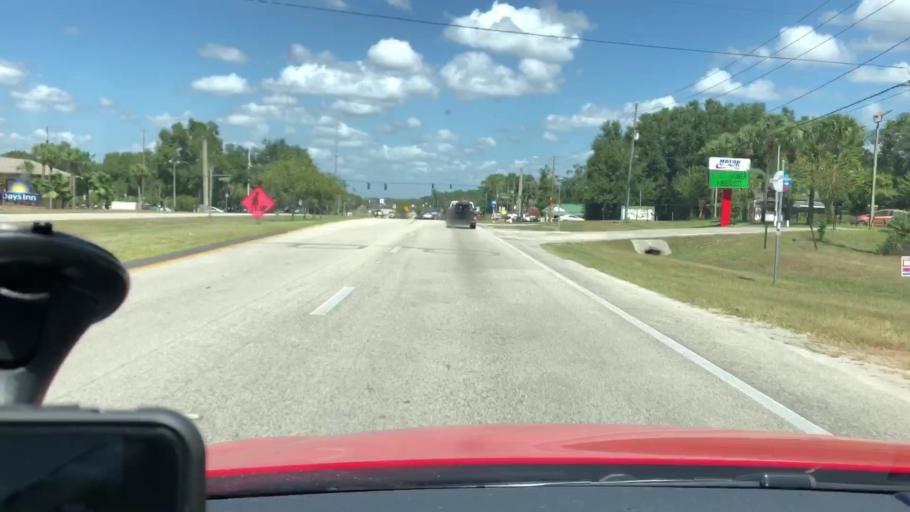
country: US
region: Florida
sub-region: Volusia County
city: Orange City
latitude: 28.9685
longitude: -81.2986
